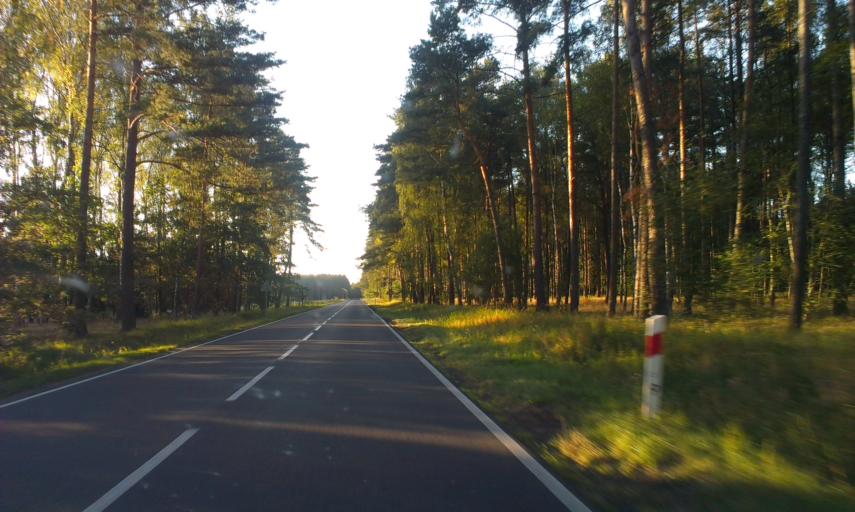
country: PL
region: Pomeranian Voivodeship
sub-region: Powiat czluchowski
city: Czarne
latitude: 53.7100
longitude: 16.8569
